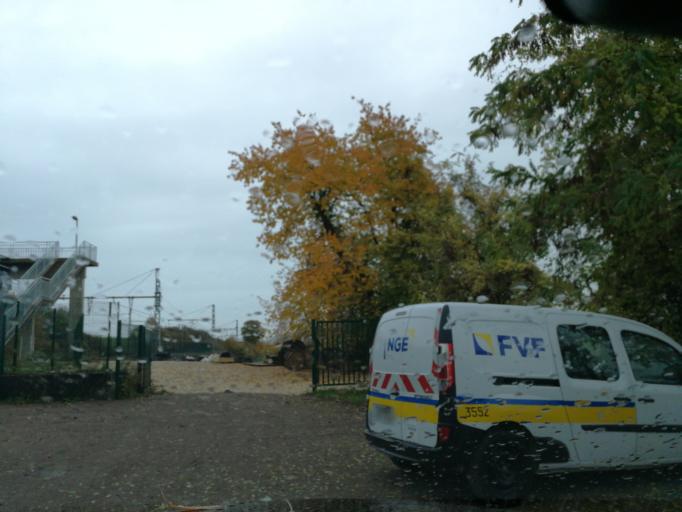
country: FR
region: Bourgogne
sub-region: Departement de la Cote-d'Or
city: Fleurey-sur-Ouche
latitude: 47.3269
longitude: 4.8102
